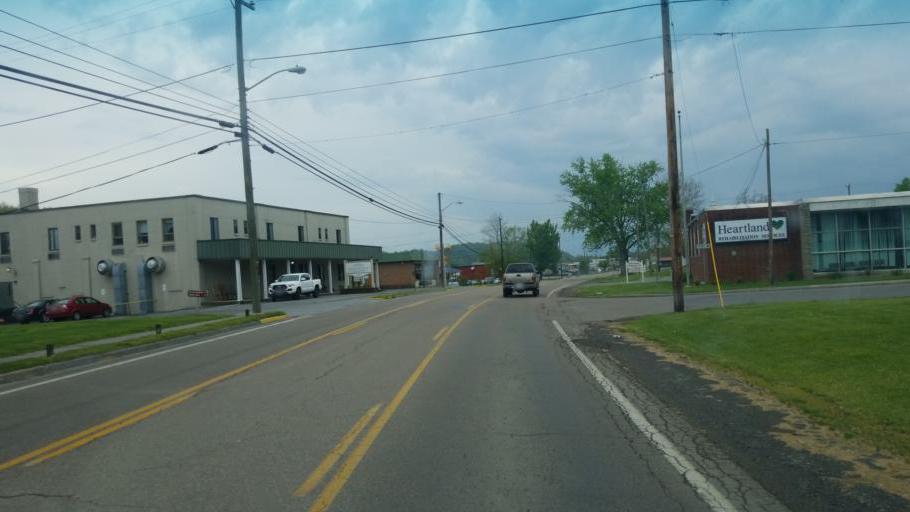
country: US
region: Virginia
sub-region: Smyth County
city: Chilhowie
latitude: 36.8036
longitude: -81.6754
